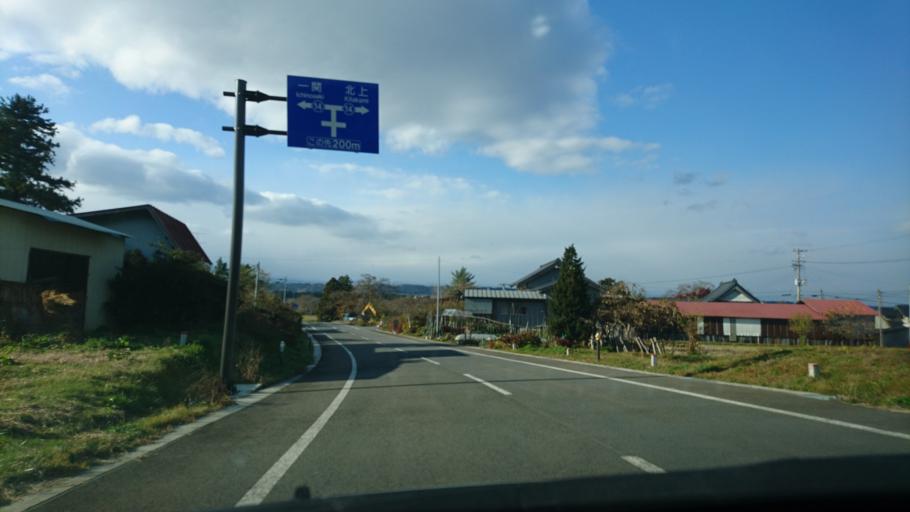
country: JP
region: Iwate
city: Mizusawa
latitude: 39.0350
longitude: 141.1535
